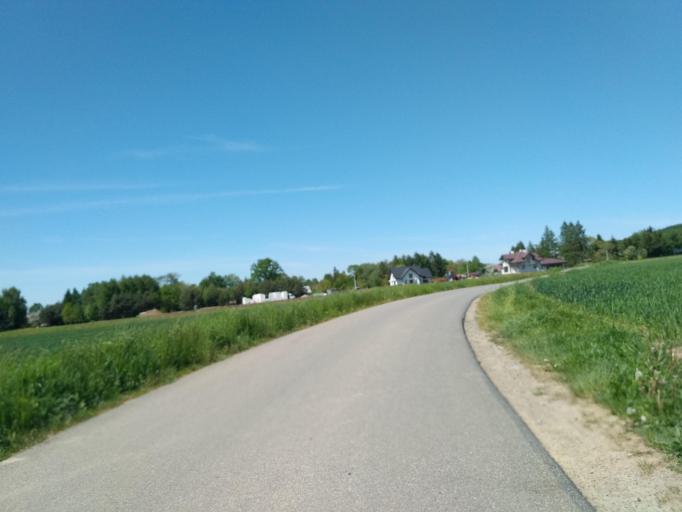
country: PL
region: Subcarpathian Voivodeship
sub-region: Powiat brzozowski
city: Gorki
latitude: 49.6159
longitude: 22.0224
